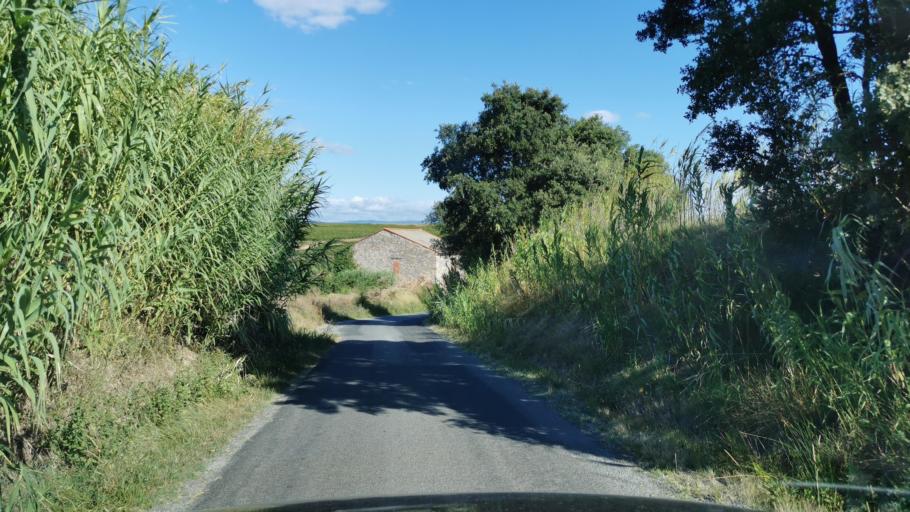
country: FR
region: Languedoc-Roussillon
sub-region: Departement de l'Aude
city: Ginestas
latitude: 43.2619
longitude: 2.8444
